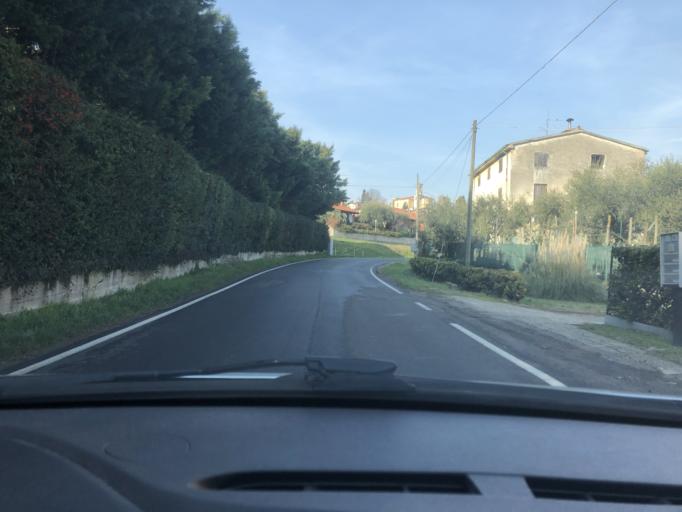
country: IT
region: Veneto
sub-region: Provincia di Verona
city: Sona
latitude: 45.4505
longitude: 10.8241
